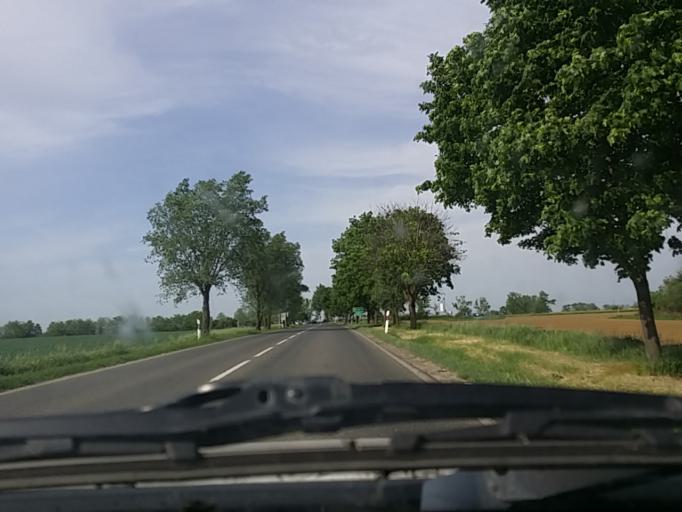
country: HU
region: Baranya
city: Harkany
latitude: 45.9154
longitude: 18.2320
